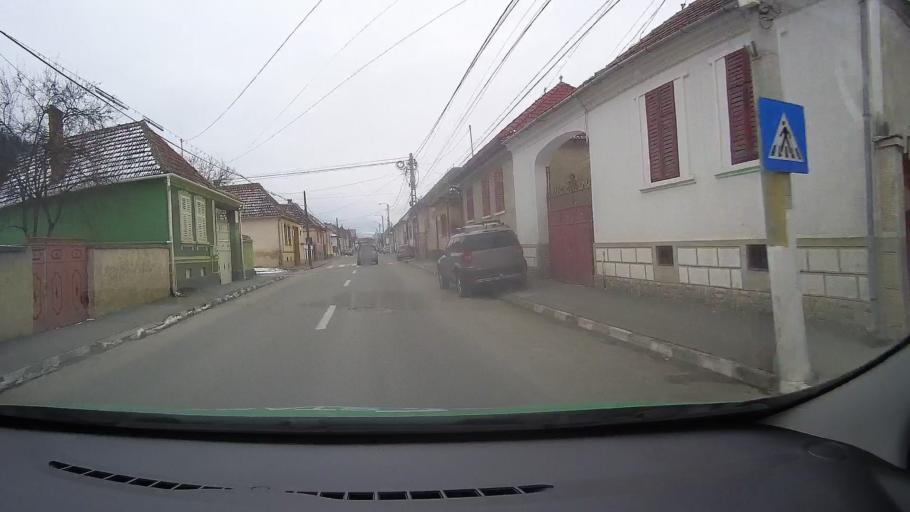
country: RO
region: Brasov
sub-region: Oras Rasnov
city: Rasnov
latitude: 45.5806
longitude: 25.4581
